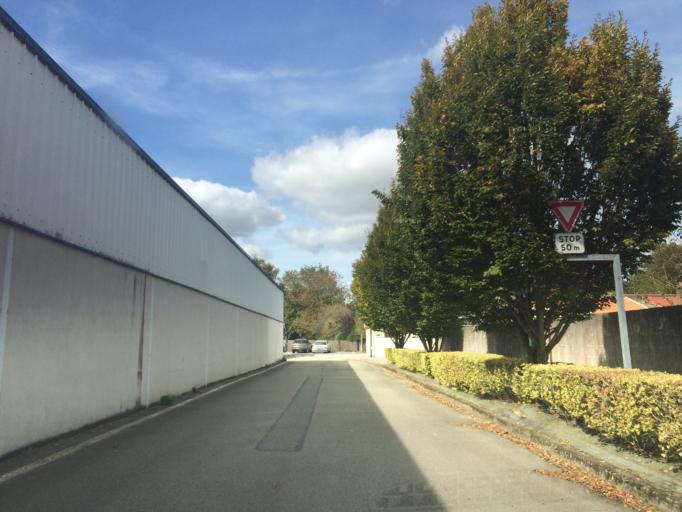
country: FR
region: Pays de la Loire
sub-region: Departement de la Loire-Atlantique
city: Chemere
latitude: 47.1232
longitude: -1.9111
